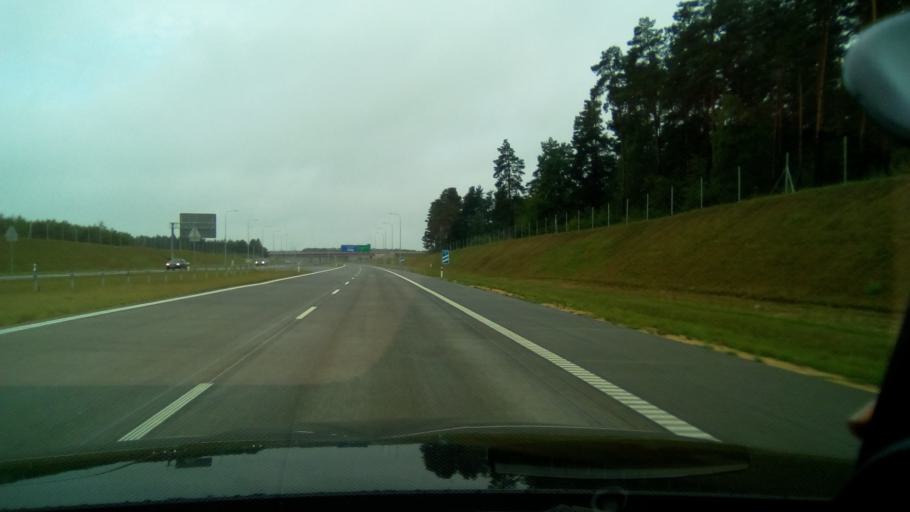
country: PL
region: Silesian Voivodeship
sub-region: Powiat klobucki
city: Kamyk
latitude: 50.8528
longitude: 19.0480
